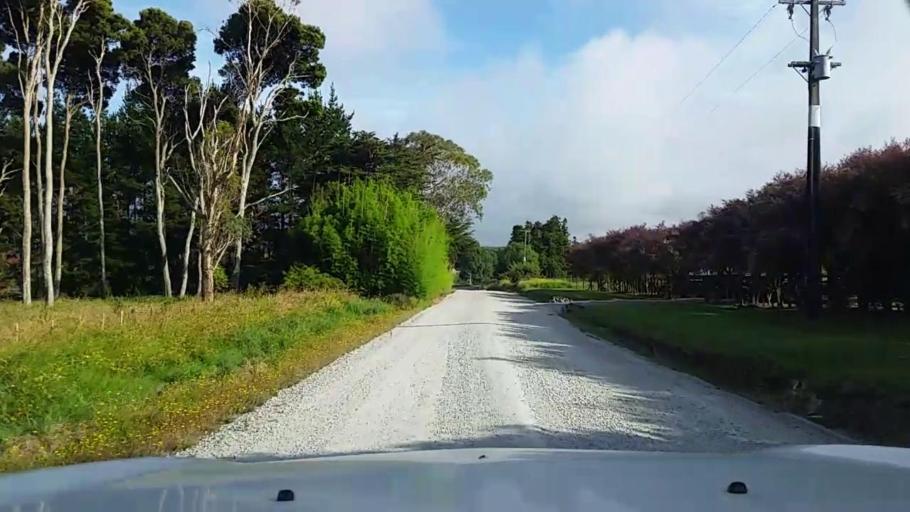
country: NZ
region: Northland
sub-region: Whangarei
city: Maungatapere
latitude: -35.6818
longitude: 174.1789
